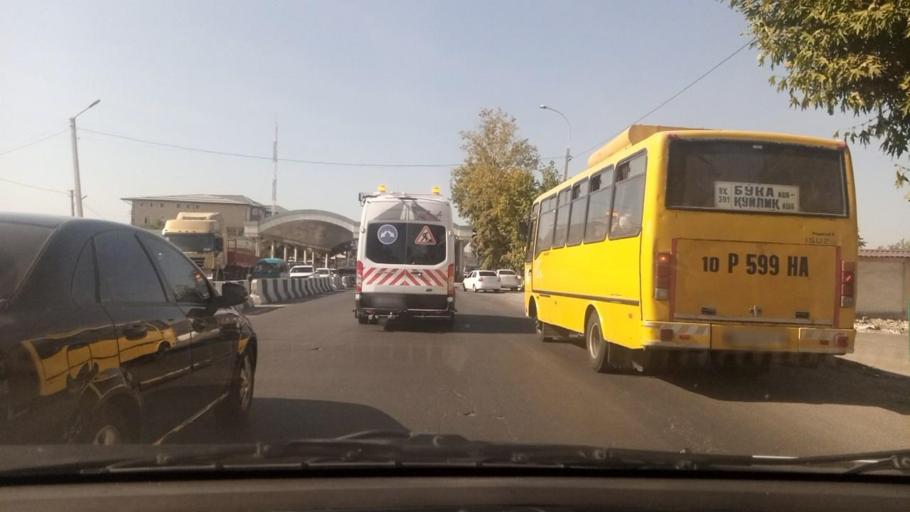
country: UZ
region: Toshkent Shahri
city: Bektemir
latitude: 41.2268
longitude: 69.3355
